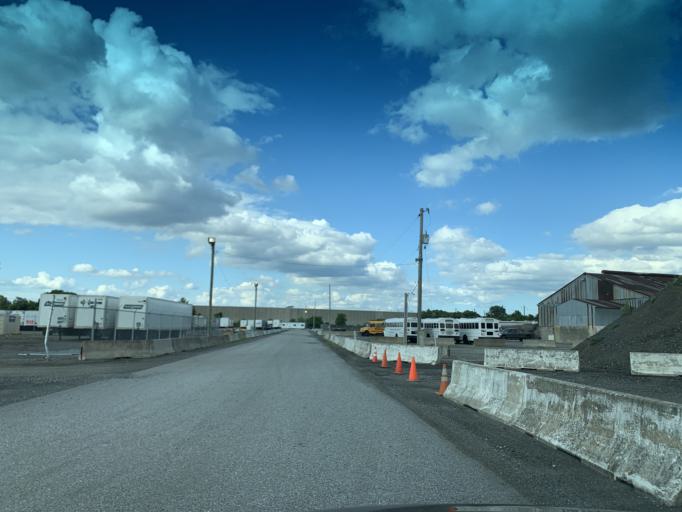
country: US
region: Maryland
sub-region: Harford County
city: Perryman
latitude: 39.4851
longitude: -76.1843
